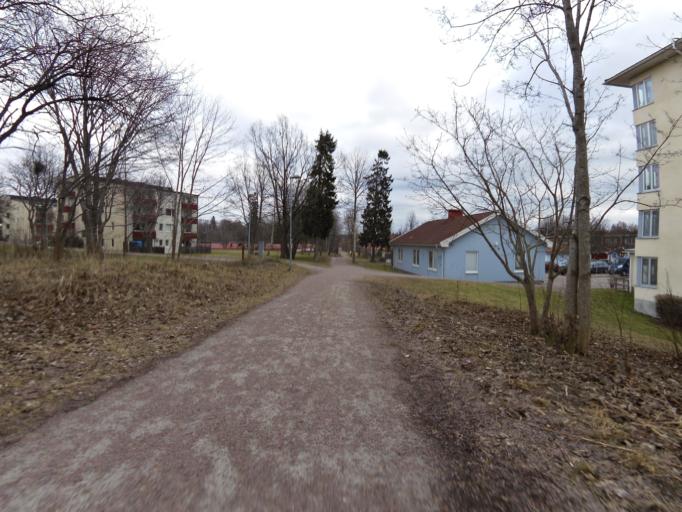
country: SE
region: Gaevleborg
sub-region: Gavle Kommun
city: Gavle
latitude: 60.6727
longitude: 17.1762
